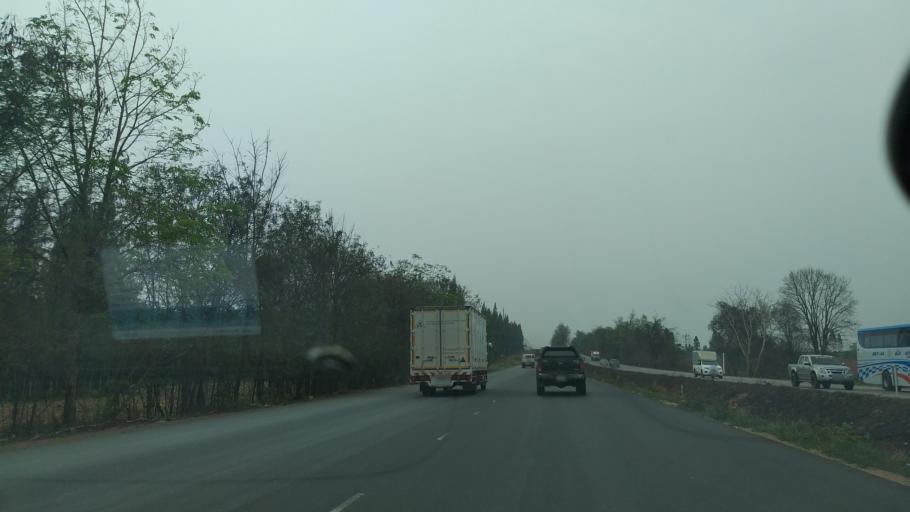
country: TH
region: Chachoengsao
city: Plaeng Yao
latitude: 13.5148
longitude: 101.2673
